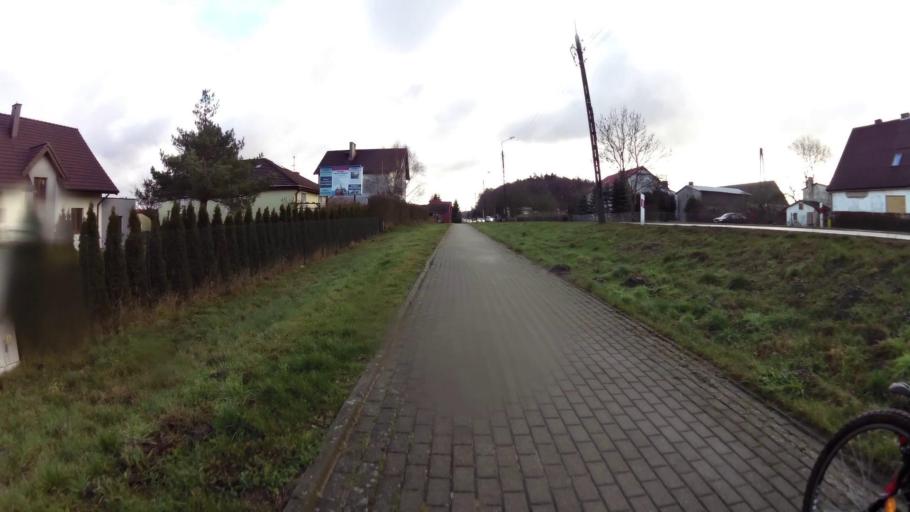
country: PL
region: West Pomeranian Voivodeship
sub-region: Powiat koszalinski
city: Sianow
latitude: 54.1305
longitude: 16.2920
